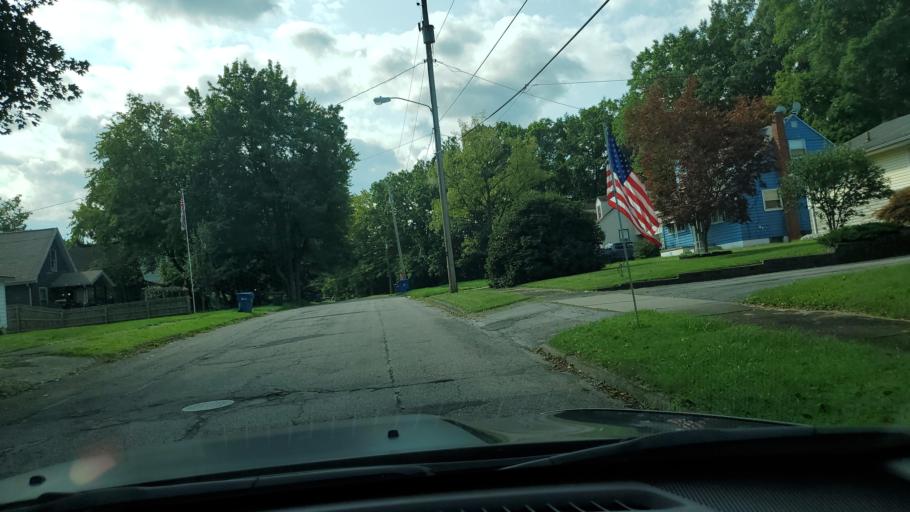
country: US
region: Ohio
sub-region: Mahoning County
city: Struthers
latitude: 41.0516
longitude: -80.5887
